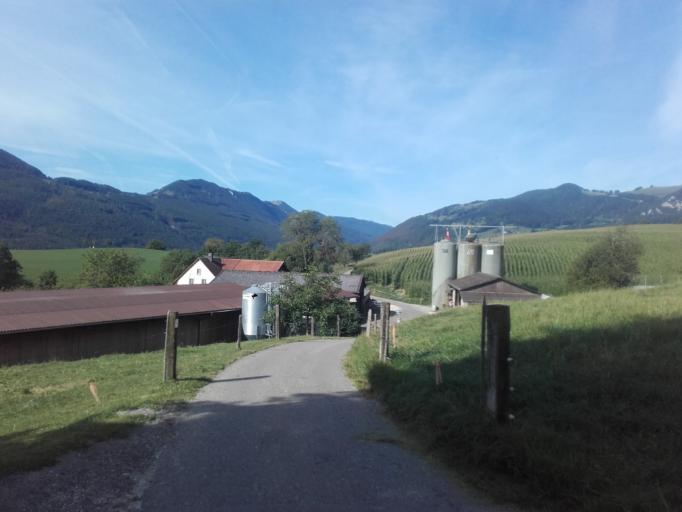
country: CH
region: Solothurn
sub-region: Bezirk Thal
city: Matzendorf
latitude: 47.3146
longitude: 7.6312
